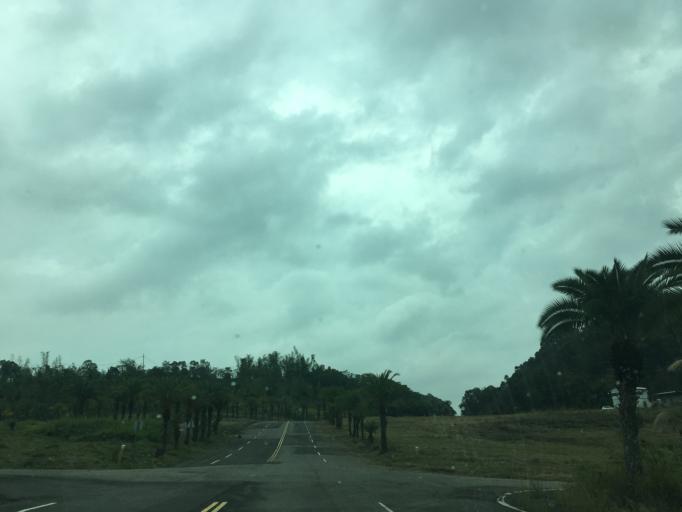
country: TW
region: Taiwan
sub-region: Taichung City
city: Taichung
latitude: 24.0597
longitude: 120.7269
